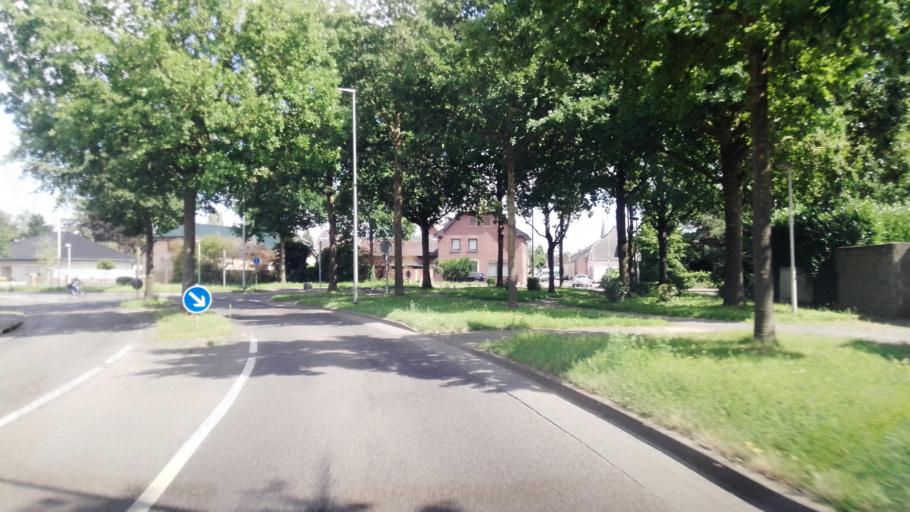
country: NL
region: Limburg
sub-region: Gemeente Venlo
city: Venlo
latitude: 51.3222
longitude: 6.1899
